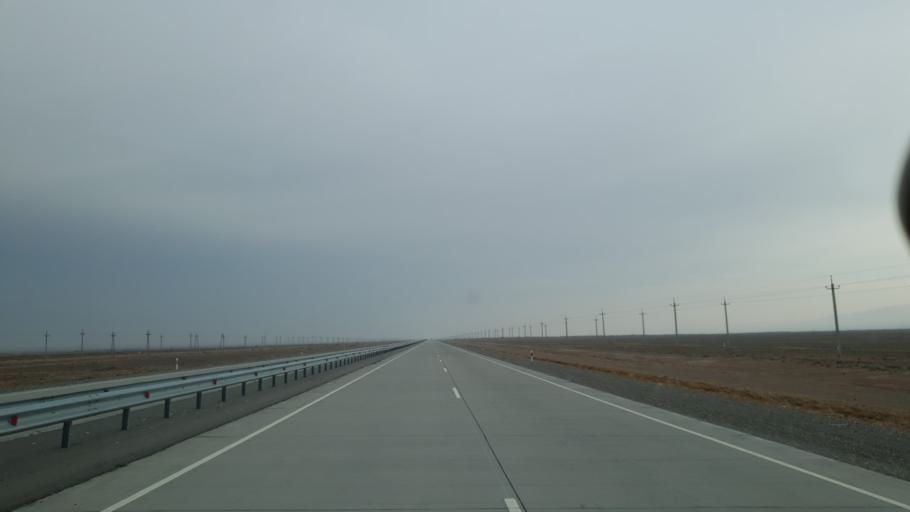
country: KZ
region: Almaty Oblysy
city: Kegen
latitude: 43.7239
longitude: 78.7574
